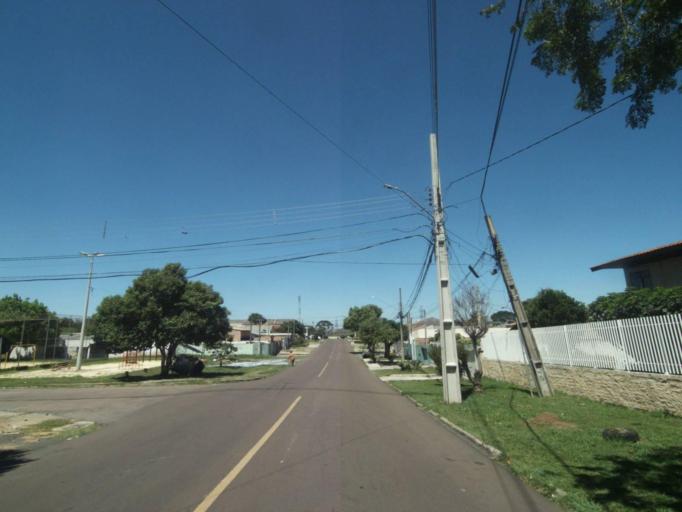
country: BR
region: Parana
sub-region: Curitiba
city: Curitiba
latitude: -25.4799
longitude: -49.3462
